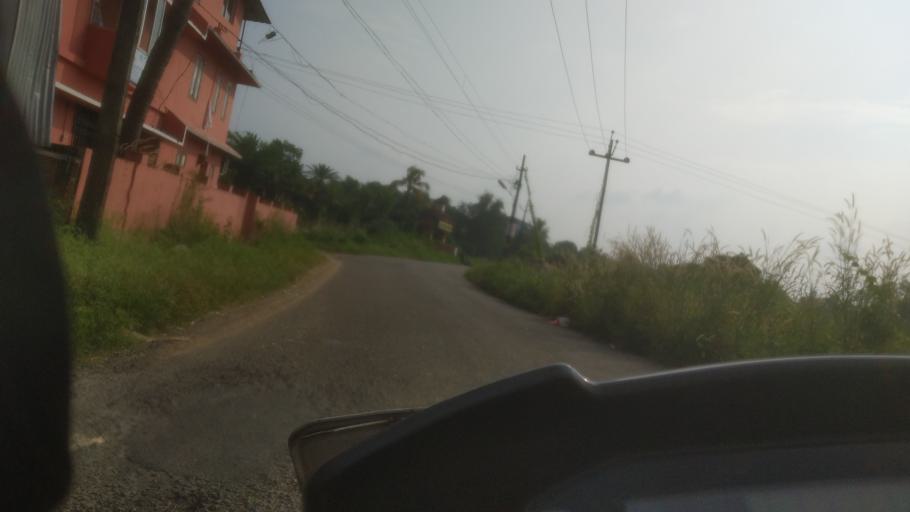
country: IN
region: Kerala
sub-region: Ernakulam
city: Angamali
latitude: 10.1615
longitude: 76.3836
